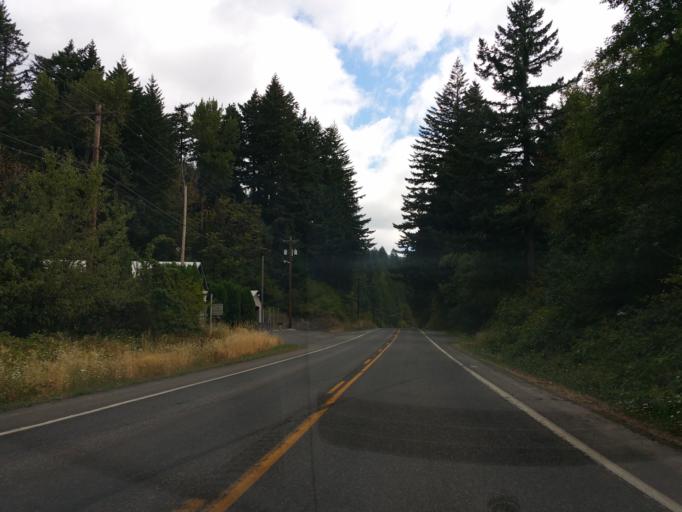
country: US
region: Washington
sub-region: Clark County
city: Washougal
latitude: 45.5952
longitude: -122.1325
